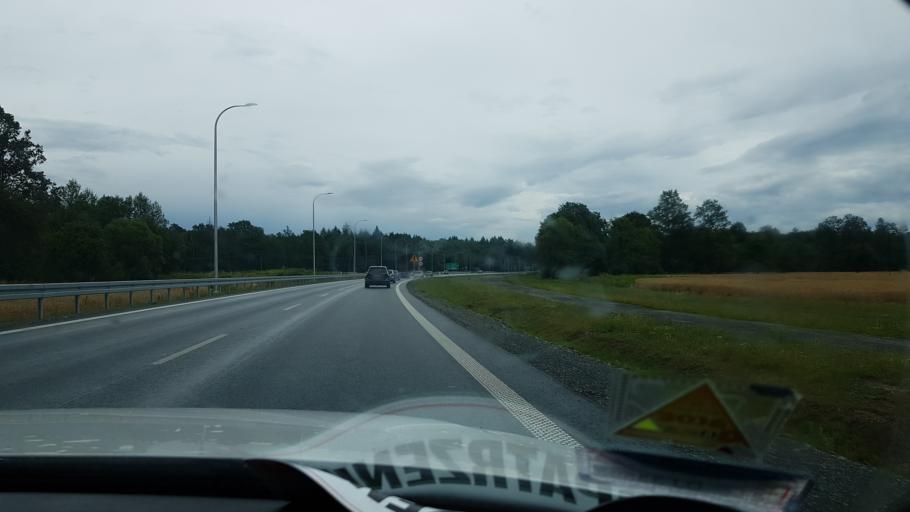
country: PL
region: Lower Silesian Voivodeship
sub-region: Powiat jeleniogorski
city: Janowice Wielkie
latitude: 50.9023
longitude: 15.8612
